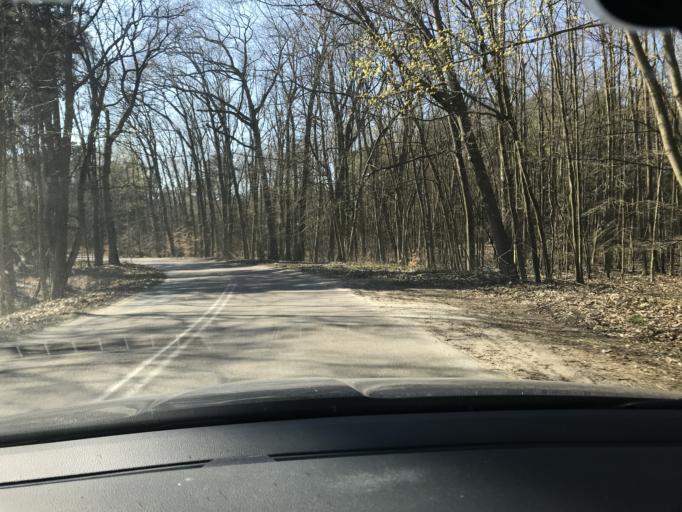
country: PL
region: Pomeranian Voivodeship
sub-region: Powiat nowodworski
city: Krynica Morska
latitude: 54.3680
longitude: 19.3988
